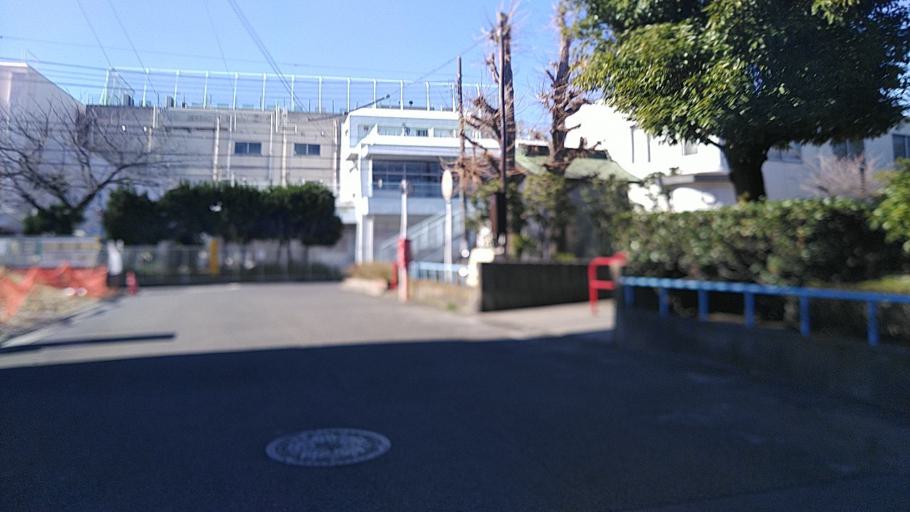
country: JP
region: Kanagawa
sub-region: Kawasaki-shi
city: Kawasaki
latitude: 35.5701
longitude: 139.7421
